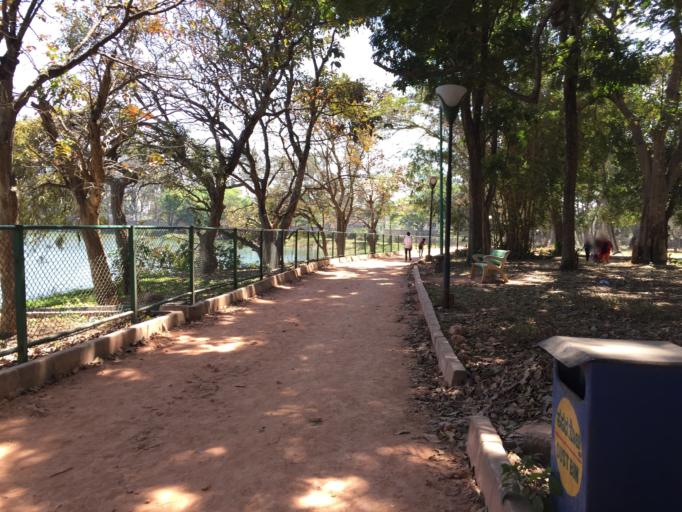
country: IN
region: Karnataka
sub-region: Bangalore Urban
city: Bangalore
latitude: 12.9455
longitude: 77.5815
